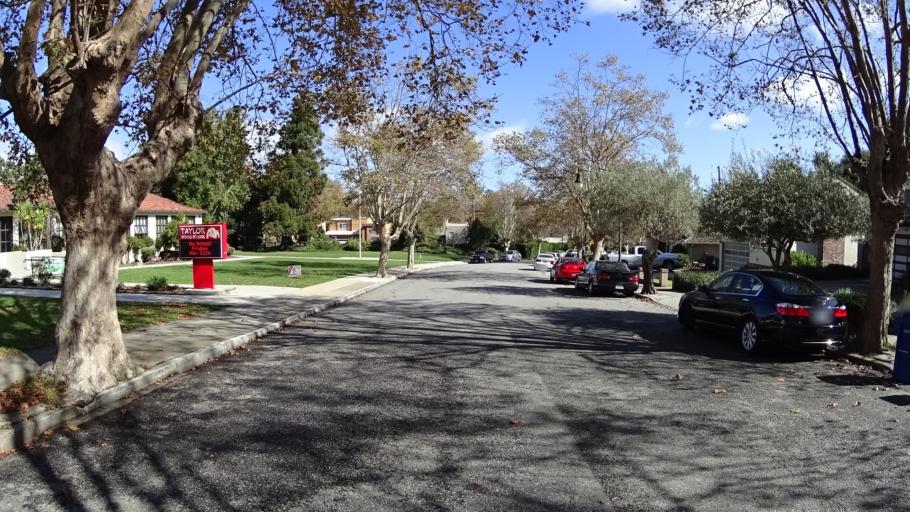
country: US
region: California
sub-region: San Mateo County
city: Millbrae
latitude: 37.5975
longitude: -122.4011
